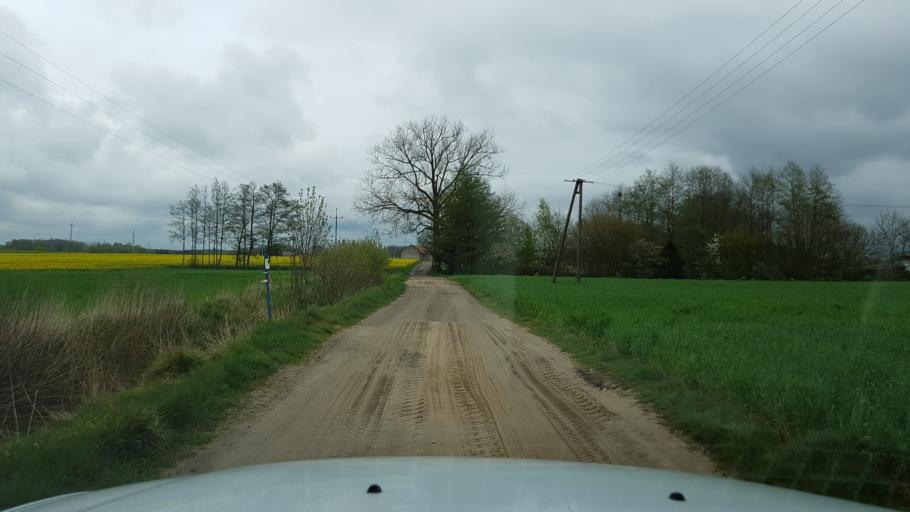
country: PL
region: West Pomeranian Voivodeship
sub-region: Powiat kolobrzeski
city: Ryman
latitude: 54.0341
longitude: 15.4749
